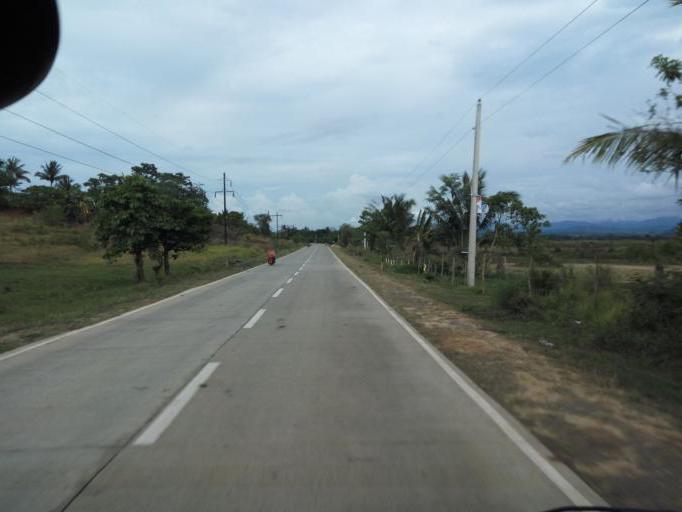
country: PH
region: Cagayan Valley
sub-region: Province of Cagayan
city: Santa Teresita
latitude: 18.2282
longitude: 121.8780
